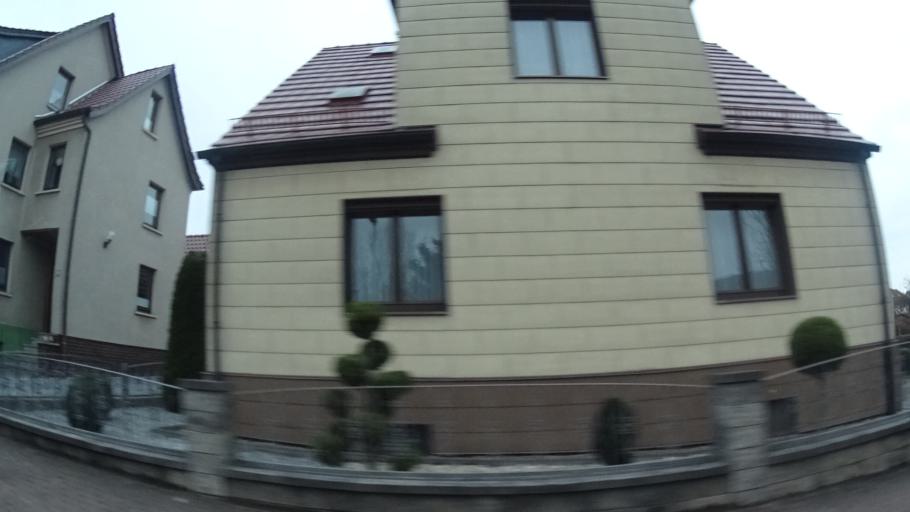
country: DE
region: Thuringia
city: Unterbreizbach
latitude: 50.7941
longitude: 9.9984
